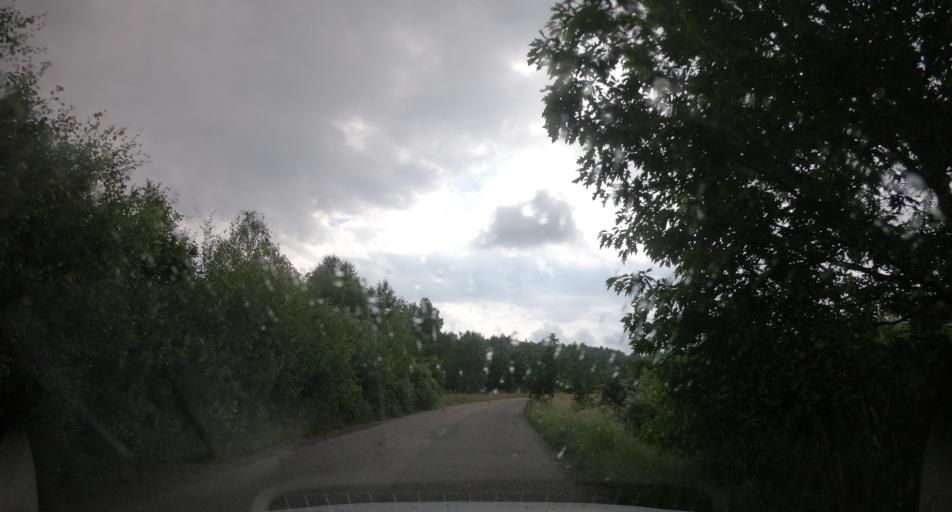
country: PL
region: West Pomeranian Voivodeship
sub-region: Powiat stargardzki
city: Insko
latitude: 53.3773
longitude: 15.6044
